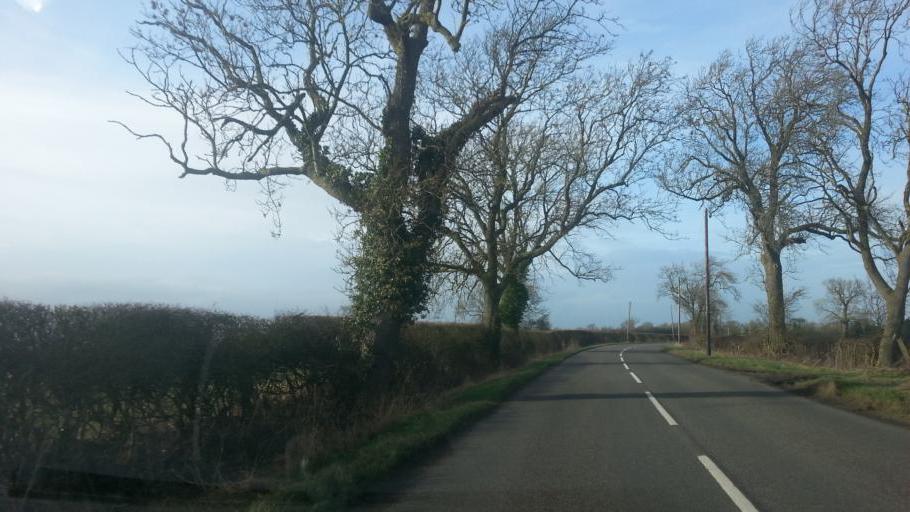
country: GB
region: England
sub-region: Leicestershire
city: Asfordby
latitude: 52.6765
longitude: -0.9402
